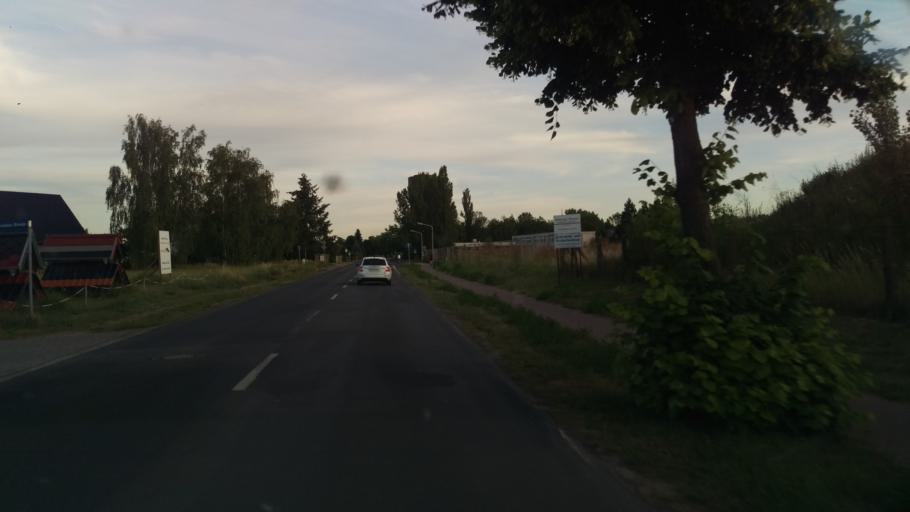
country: DE
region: Brandenburg
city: Eisenhuettenstadt
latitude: 52.1537
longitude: 14.6731
